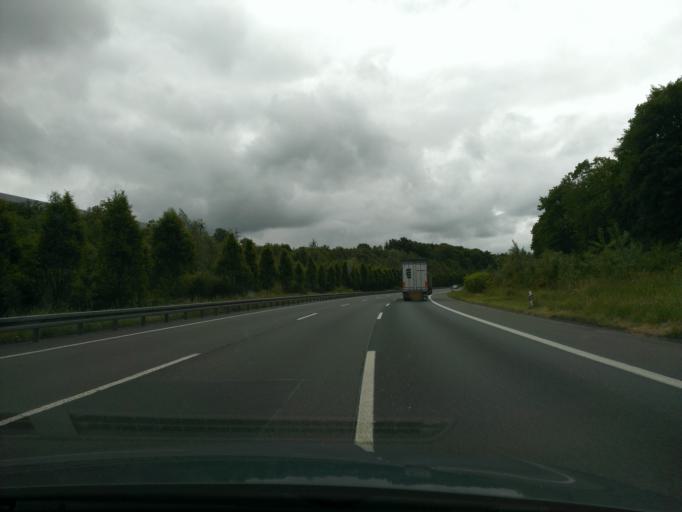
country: DE
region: North Rhine-Westphalia
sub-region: Regierungsbezirk Dusseldorf
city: Remscheid
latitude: 51.2388
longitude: 7.2303
